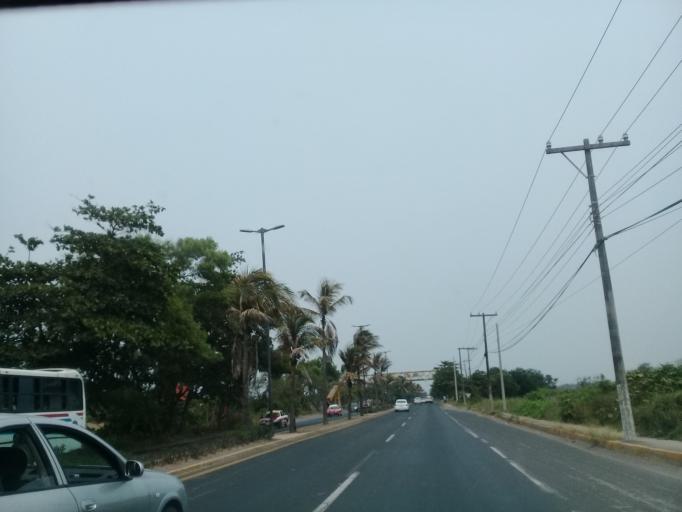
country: MX
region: Veracruz
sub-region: Veracruz
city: Hacienda Sotavento
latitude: 19.1478
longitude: -96.1689
